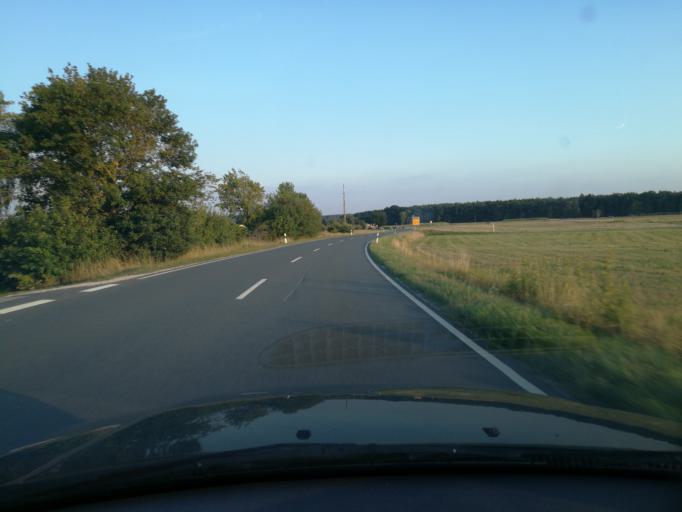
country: DE
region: Bavaria
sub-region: Regierungsbezirk Mittelfranken
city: Hessdorf
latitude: 49.6347
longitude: 10.9020
